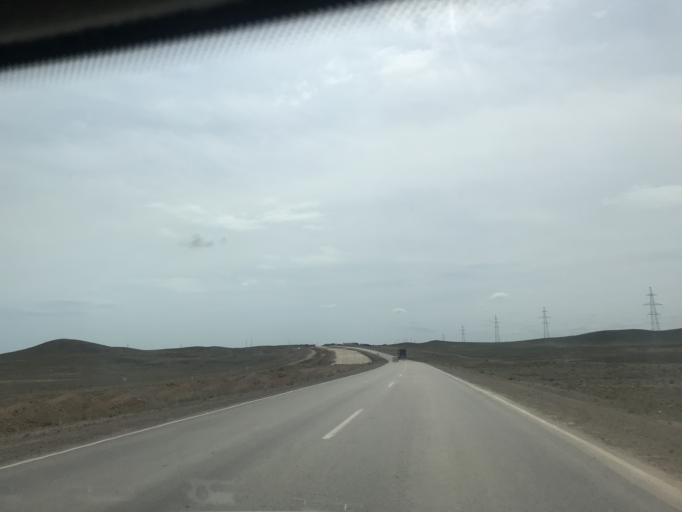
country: KZ
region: Zhambyl
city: Mynaral
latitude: 45.3492
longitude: 73.6897
